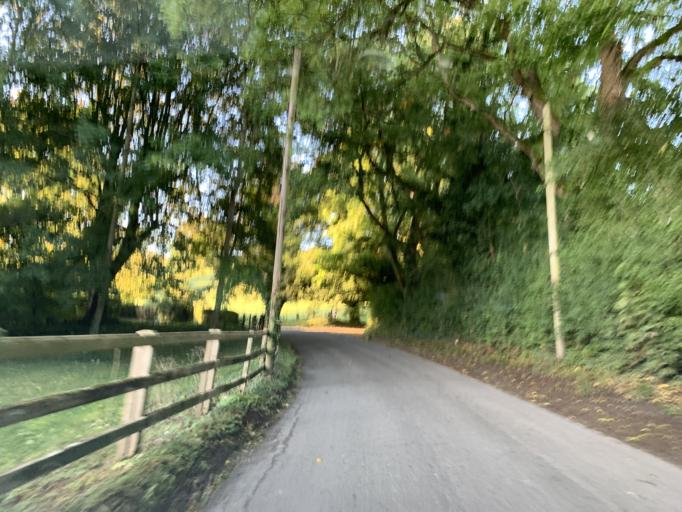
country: GB
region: England
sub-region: Wiltshire
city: Woodford
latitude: 51.1083
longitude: -1.8318
